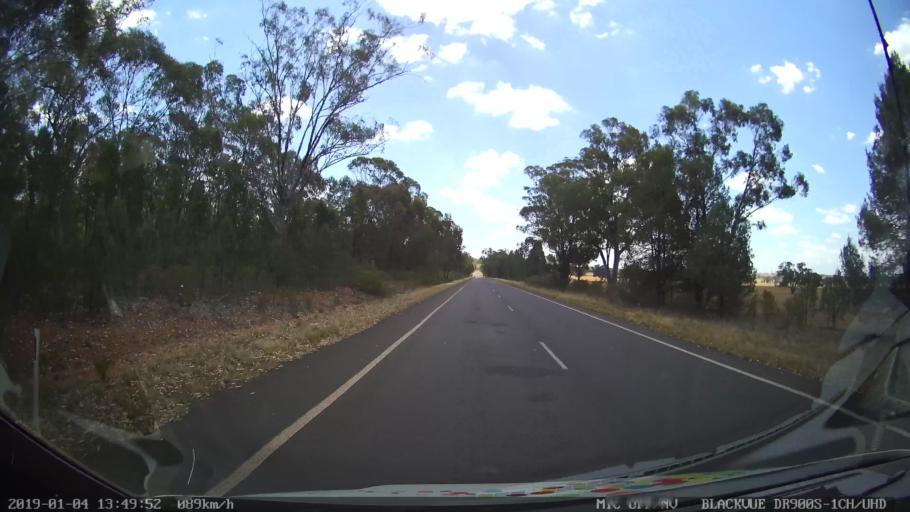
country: AU
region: New South Wales
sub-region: Dubbo Municipality
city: Dubbo
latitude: -32.4268
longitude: 148.5765
